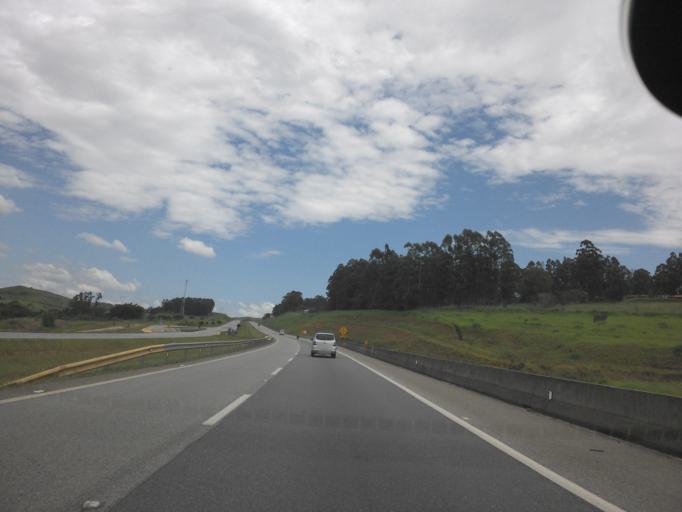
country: BR
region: Sao Paulo
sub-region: Sao Jose Dos Campos
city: Sao Jose dos Campos
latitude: -23.2362
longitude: -45.7846
